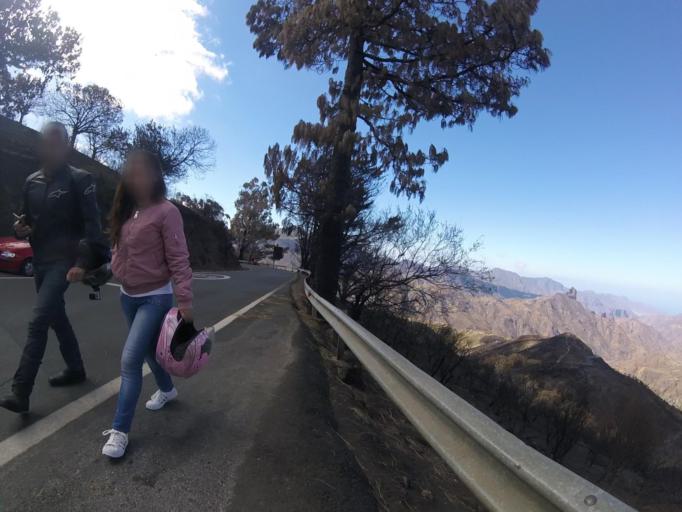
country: ES
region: Canary Islands
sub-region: Provincia de Las Palmas
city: Tejeda
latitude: 28.0057
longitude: -15.6000
